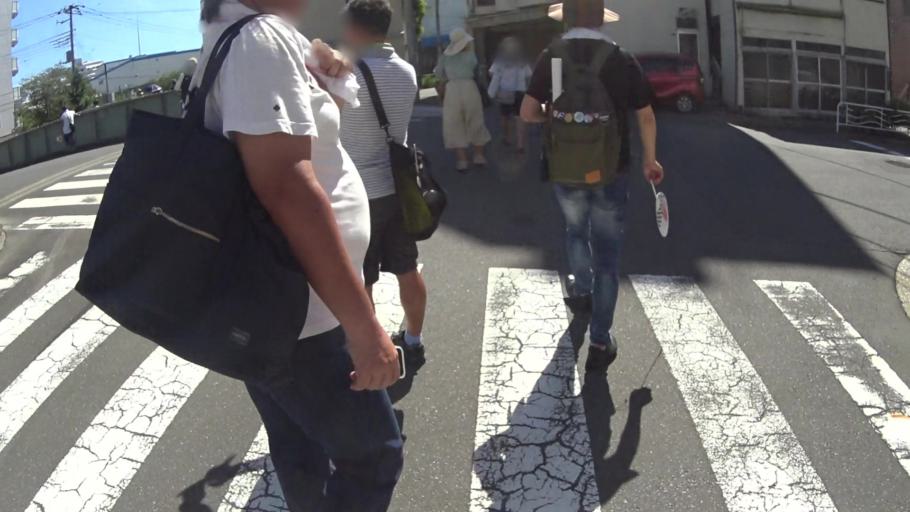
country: JP
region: Tokyo
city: Urayasu
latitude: 35.6728
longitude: 139.7911
